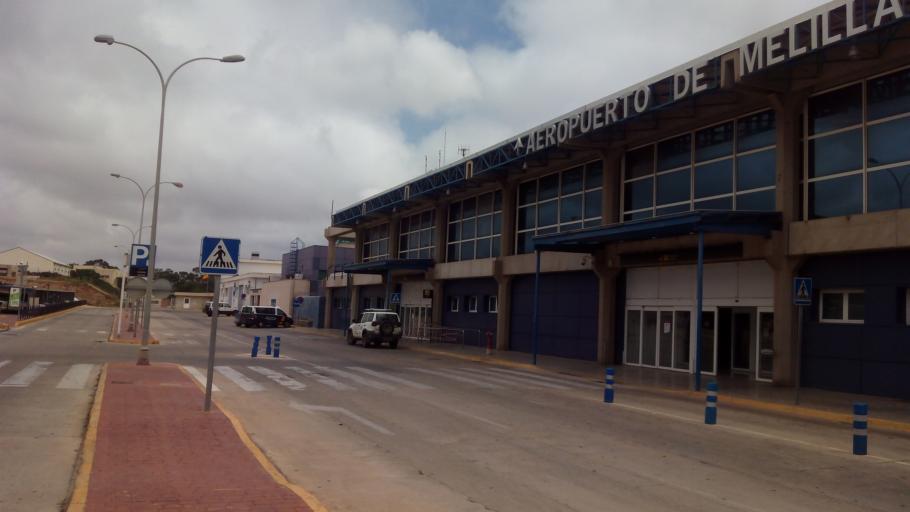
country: ES
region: Melilla
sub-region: Melilla
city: Melilla
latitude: 35.2770
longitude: -2.9576
